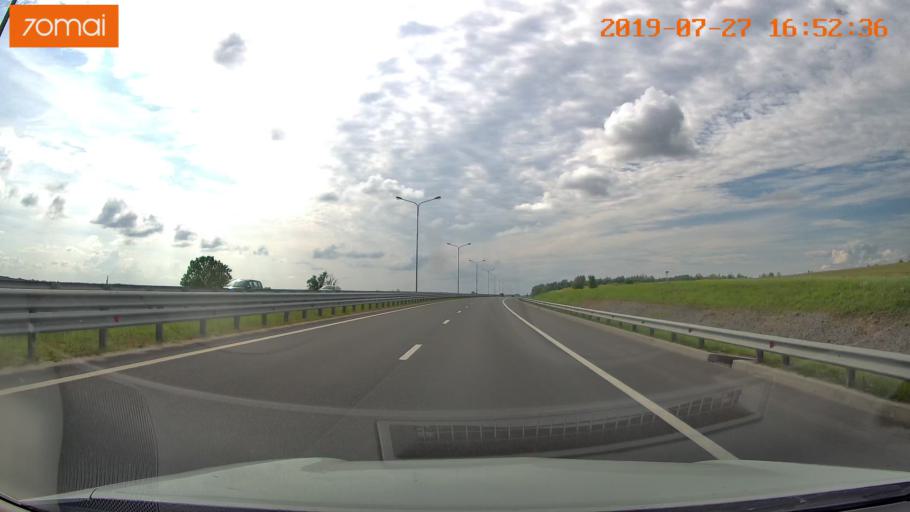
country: RU
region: Kaliningrad
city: Gvardeysk
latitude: 54.6835
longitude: 20.8529
